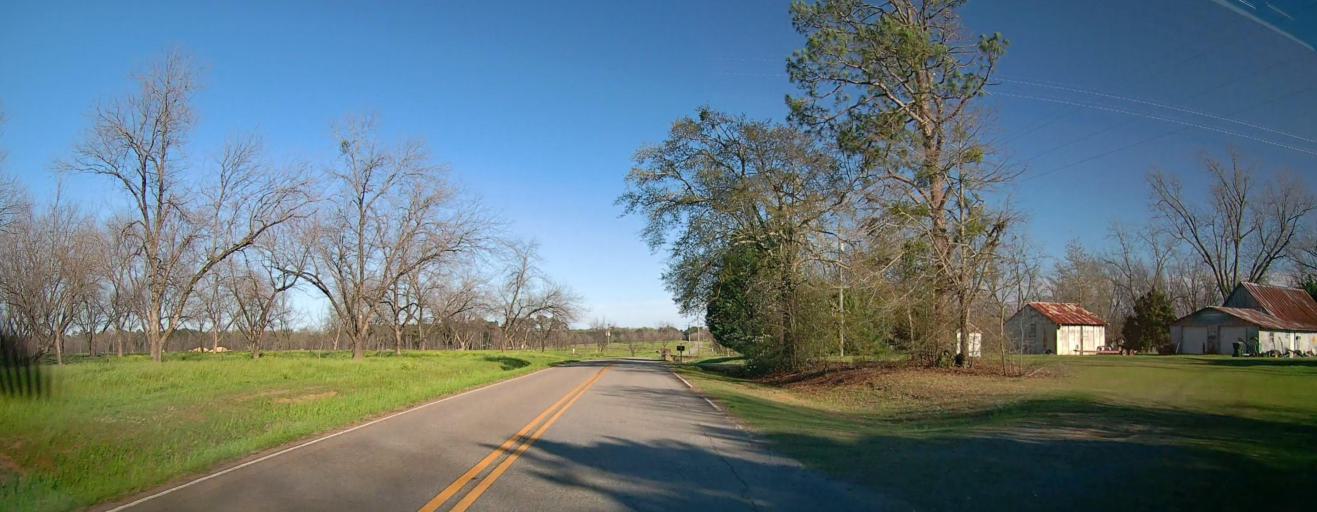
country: US
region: Georgia
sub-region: Houston County
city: Perry
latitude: 32.3675
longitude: -83.6847
